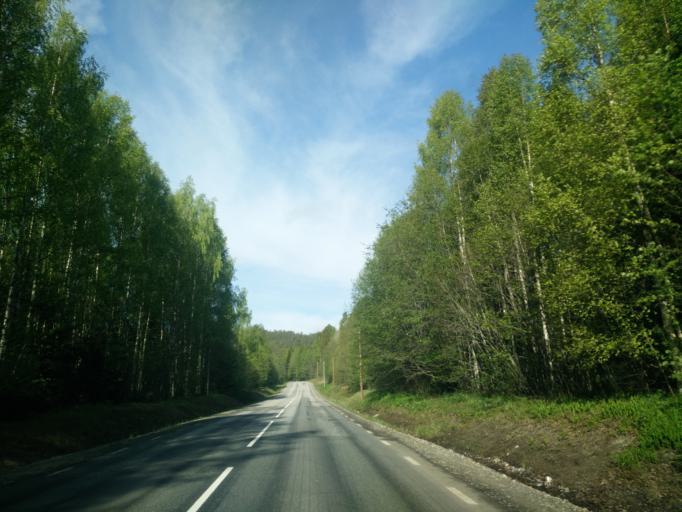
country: SE
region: Vaesternorrland
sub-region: Sundsvalls Kommun
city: Sundsvall
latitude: 62.3048
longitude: 17.2776
